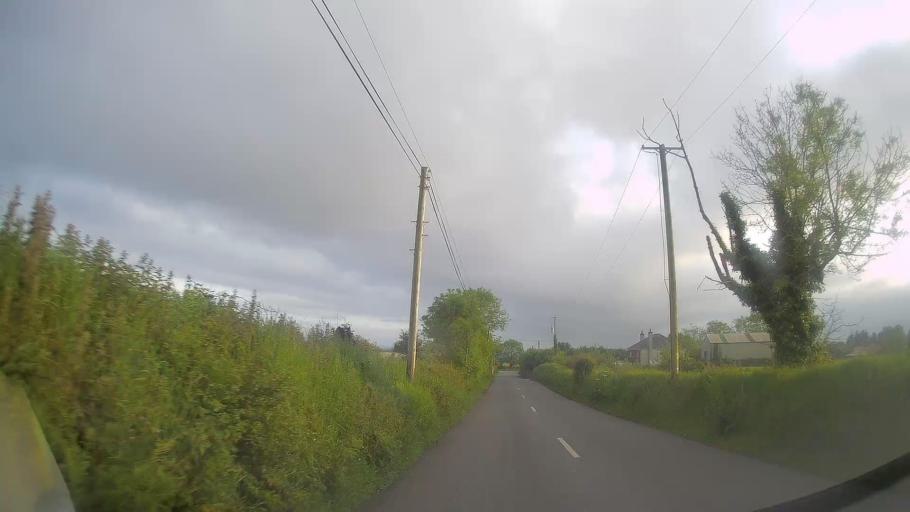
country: IE
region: Munster
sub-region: County Cork
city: Blarney
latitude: 51.9757
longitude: -8.5539
